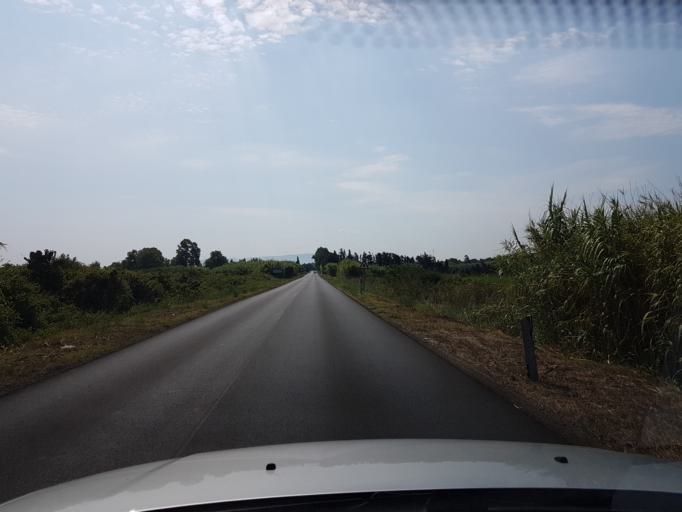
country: IT
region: Sardinia
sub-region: Provincia di Oristano
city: Donigala Fenugheddu
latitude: 39.9490
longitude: 8.5624
